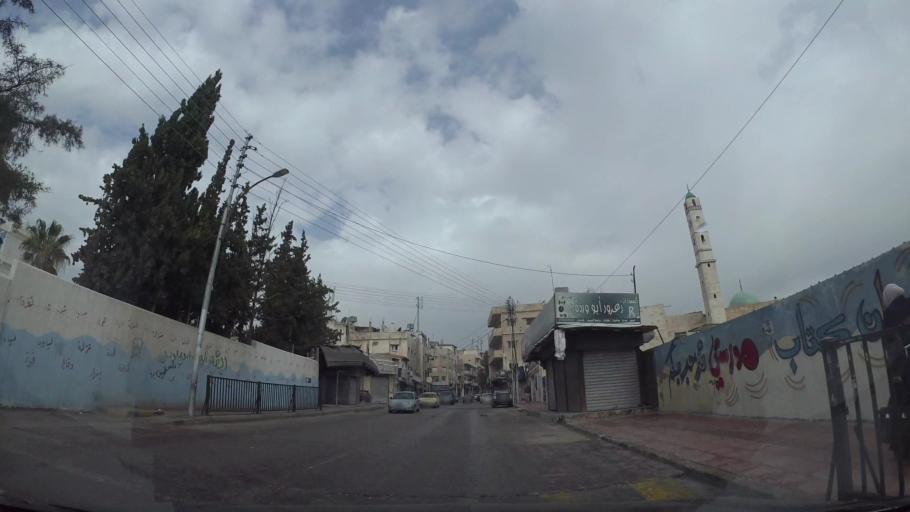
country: JO
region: Amman
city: Amman
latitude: 31.9733
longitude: 35.9268
